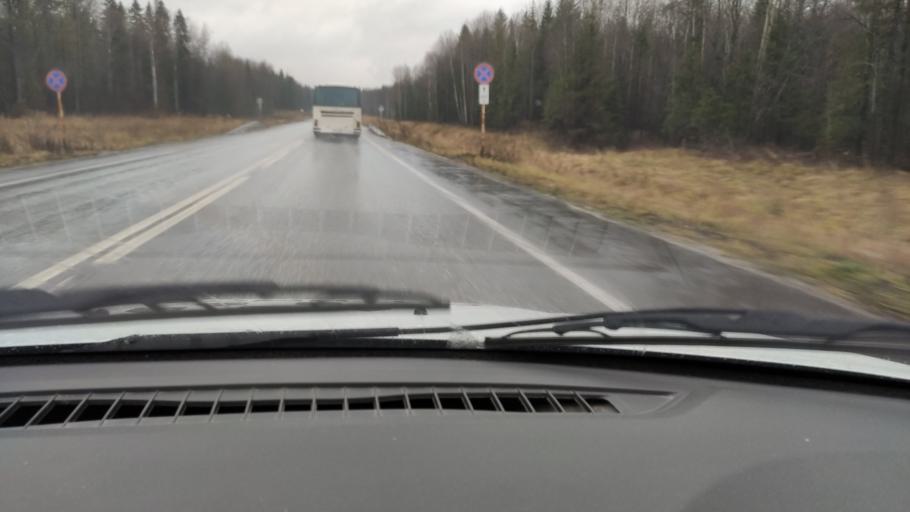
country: RU
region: Perm
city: Novyye Lyady
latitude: 58.0425
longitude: 56.5419
